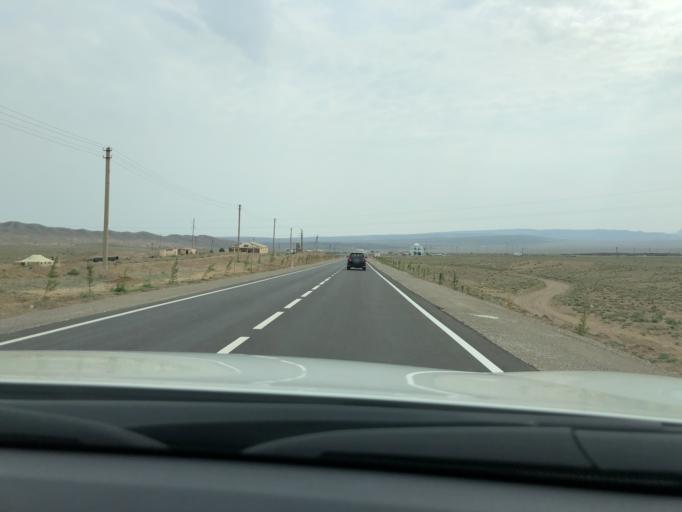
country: TJ
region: Viloyati Sughd
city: Kim
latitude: 40.1978
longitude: 70.4778
